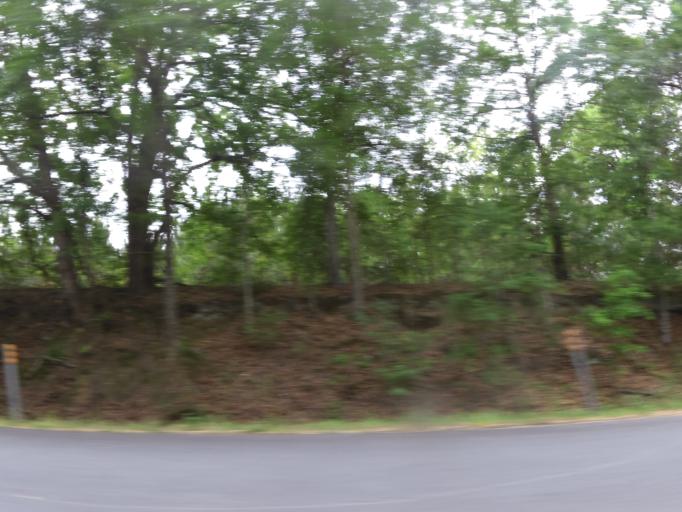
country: US
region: Georgia
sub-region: Emanuel County
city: Twin City
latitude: 32.4544
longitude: -82.2242
